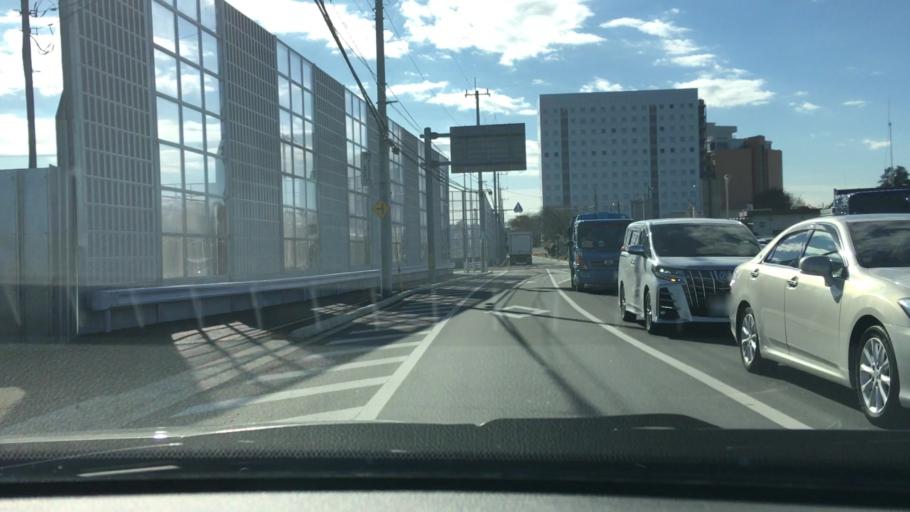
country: JP
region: Chiba
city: Narita
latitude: 35.7844
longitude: 140.3856
